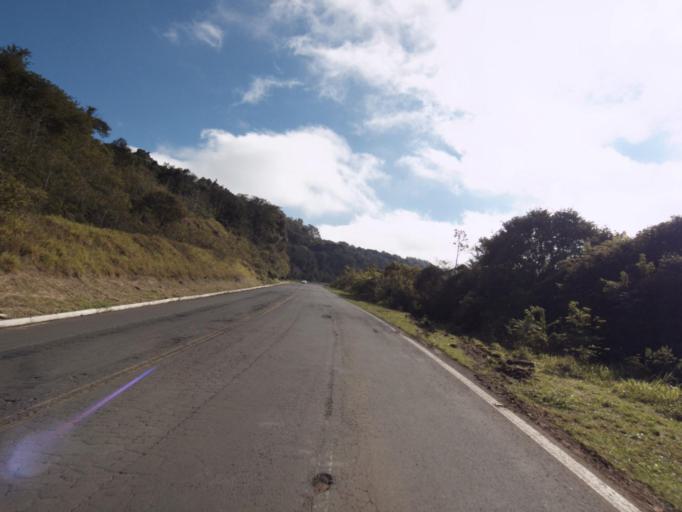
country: BR
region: Rio Grande do Sul
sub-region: Frederico Westphalen
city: Frederico Westphalen
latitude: -27.1345
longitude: -53.2126
